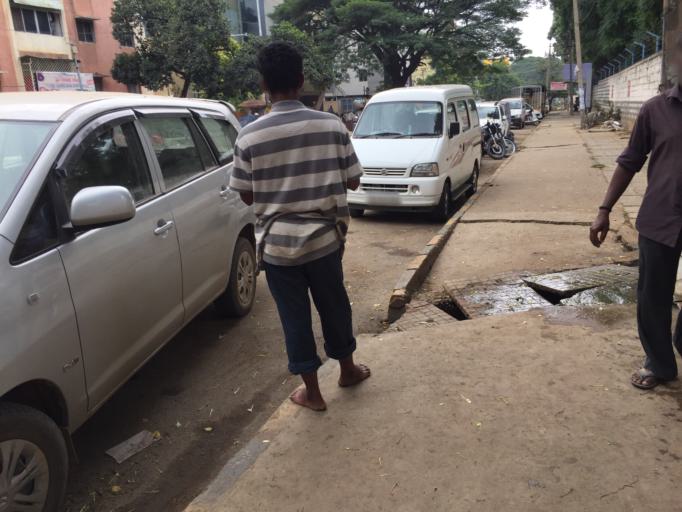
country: IN
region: Karnataka
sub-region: Bangalore Urban
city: Bangalore
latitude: 12.9579
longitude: 77.6539
